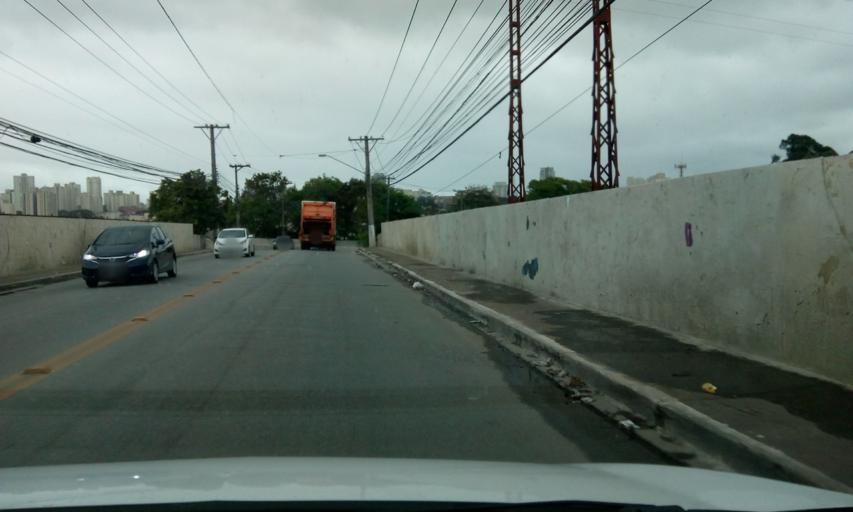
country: BR
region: Sao Paulo
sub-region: Sao Paulo
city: Sao Paulo
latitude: -23.5670
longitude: -46.6038
